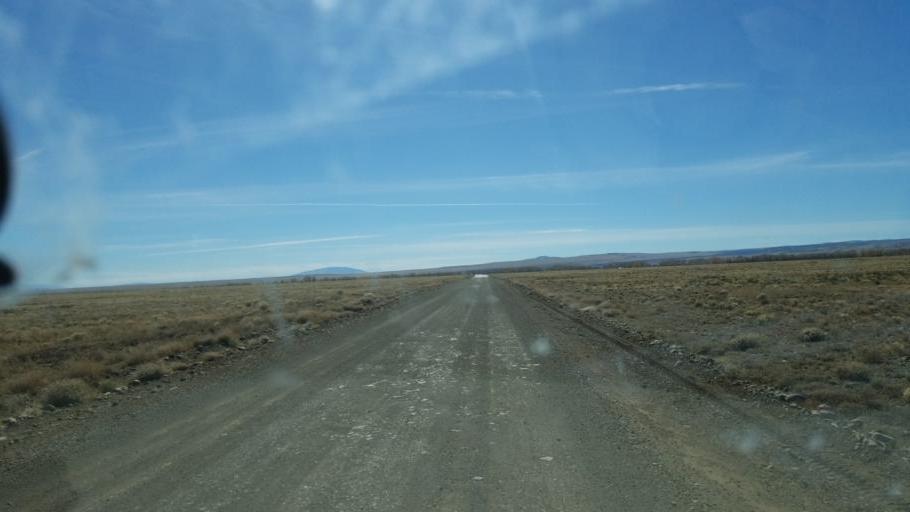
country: US
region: Colorado
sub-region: Rio Grande County
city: Monte Vista
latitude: 37.3188
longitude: -106.1488
